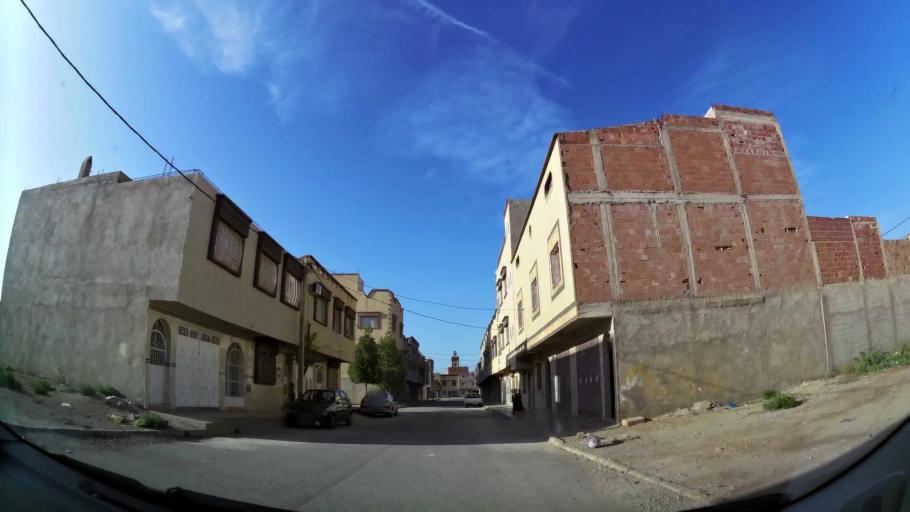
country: MA
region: Oriental
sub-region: Oujda-Angad
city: Oujda
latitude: 34.7101
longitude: -1.8991
